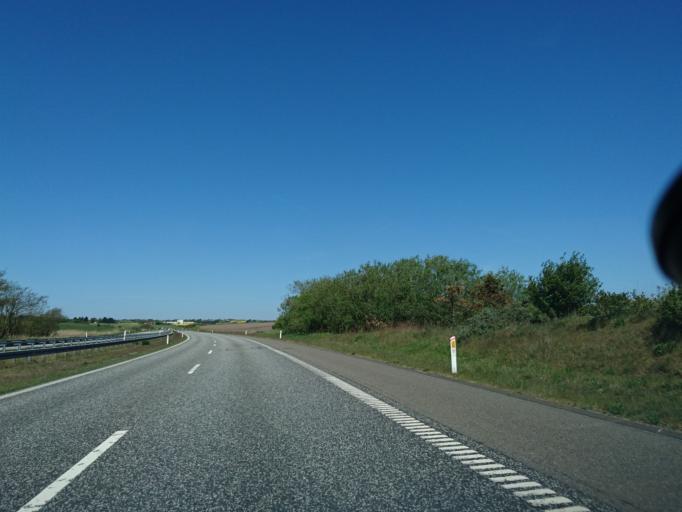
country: DK
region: North Denmark
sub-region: Hjorring Kommune
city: Hjorring
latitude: 57.5306
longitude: 10.0123
